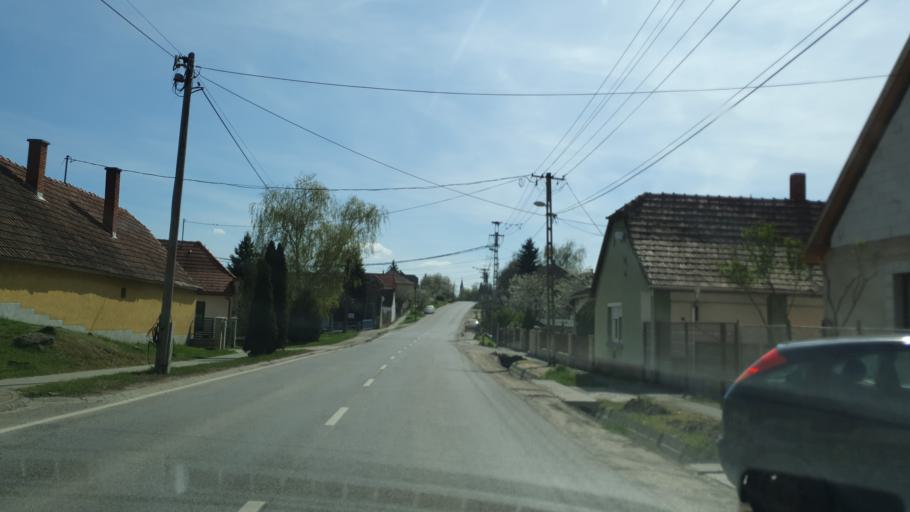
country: HU
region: Fejer
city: Pusztavam
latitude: 47.4374
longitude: 18.2328
